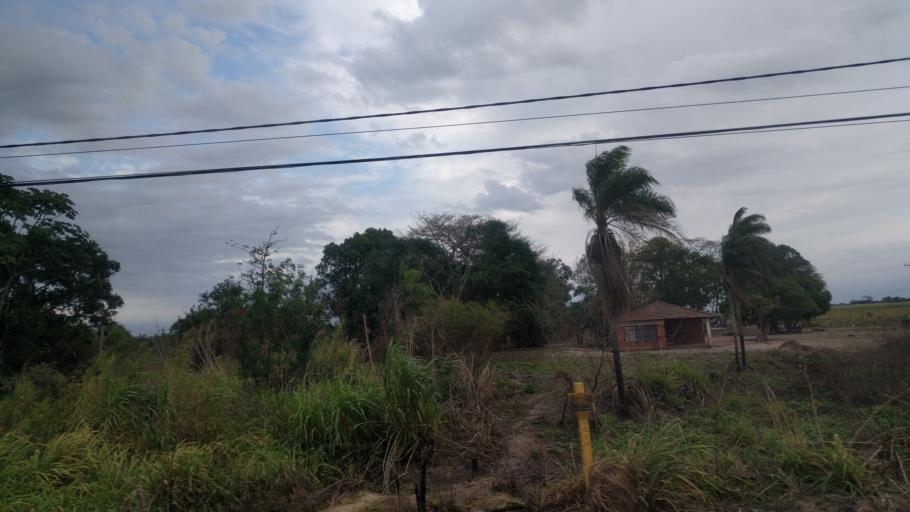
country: BO
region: Santa Cruz
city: Montero
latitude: -17.4005
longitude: -63.2092
